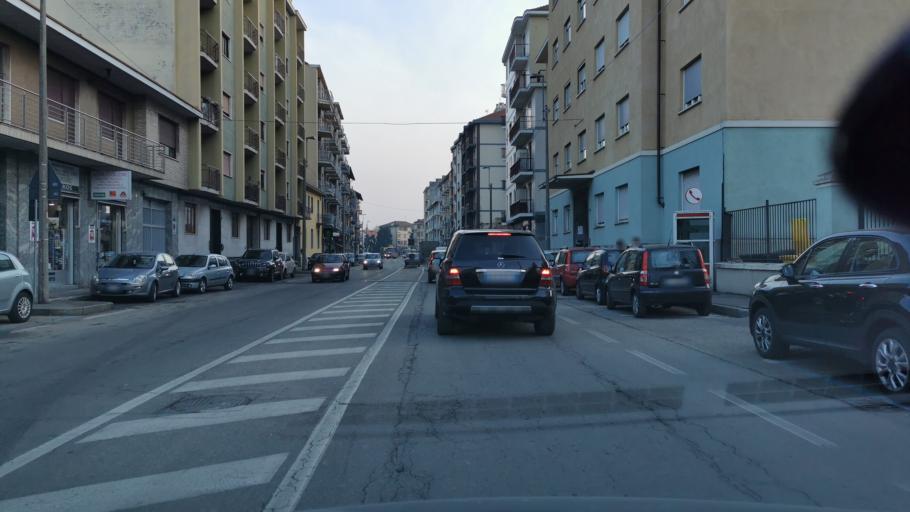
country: IT
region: Piedmont
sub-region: Provincia di Torino
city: Venaria Reale
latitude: 45.1298
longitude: 7.6346
